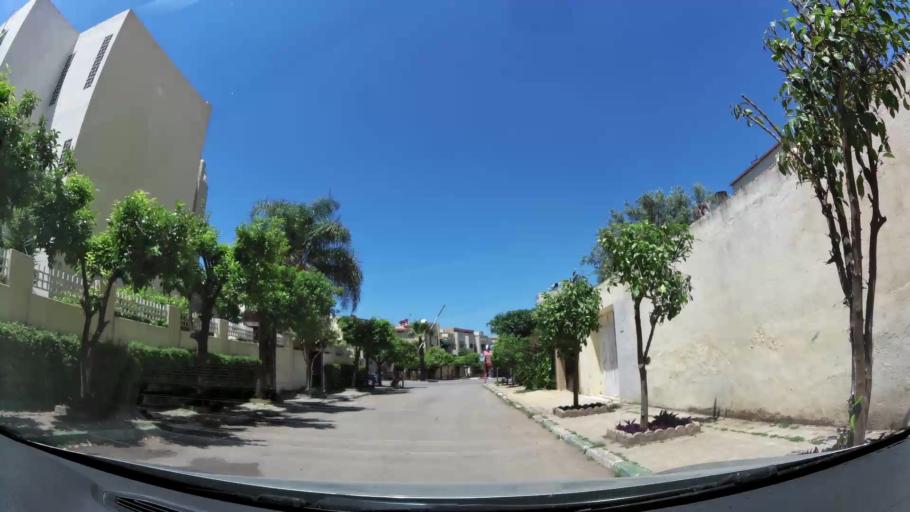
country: MA
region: Fes-Boulemane
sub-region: Fes
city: Fes
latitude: 34.0203
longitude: -5.0171
